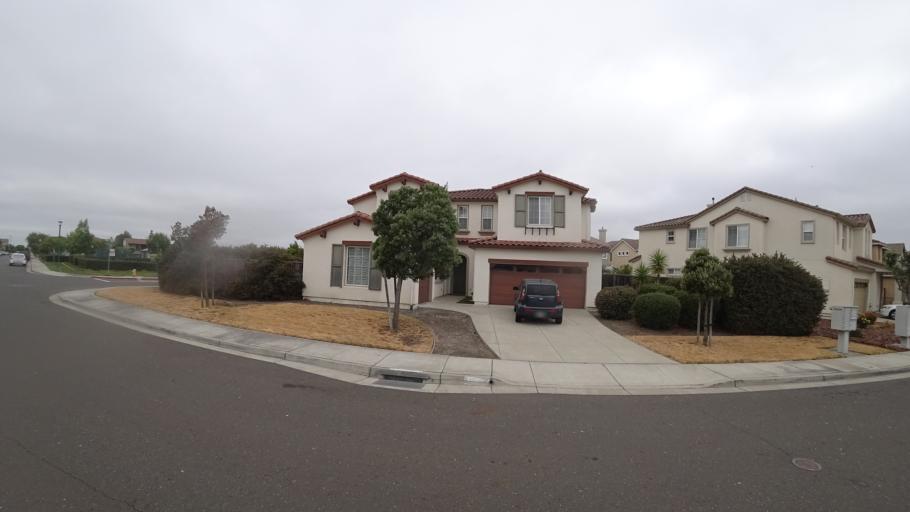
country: US
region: California
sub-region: Alameda County
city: Hayward
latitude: 37.6062
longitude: -122.0911
